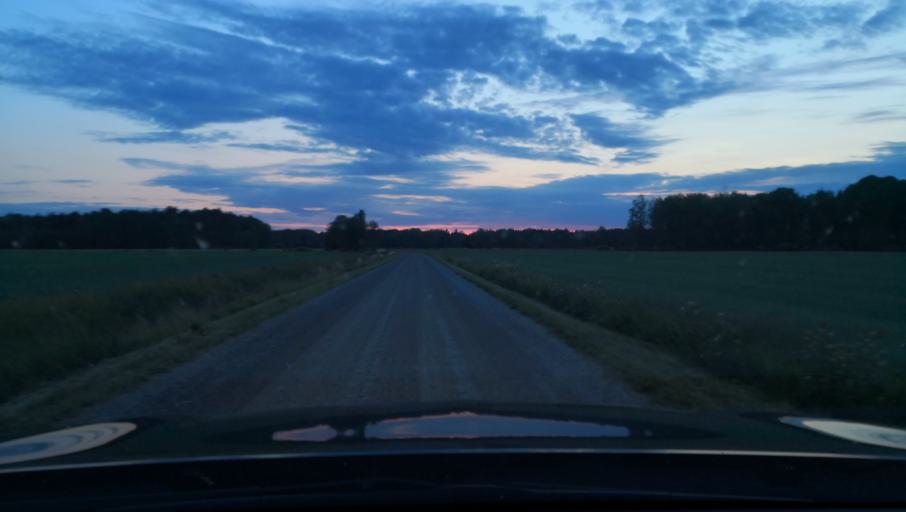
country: SE
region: Uppsala
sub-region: Heby Kommun
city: OEstervala
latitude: 60.0131
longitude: 17.3101
